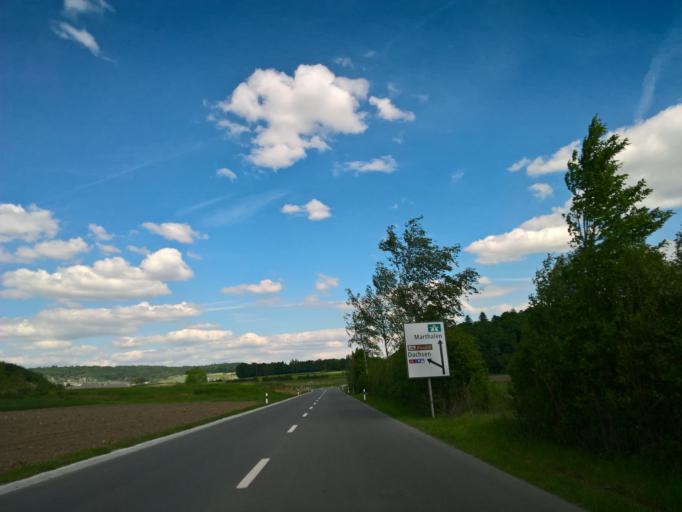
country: CH
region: Zurich
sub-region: Bezirk Andelfingen
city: Dachsen
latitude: 47.6392
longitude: 8.6256
